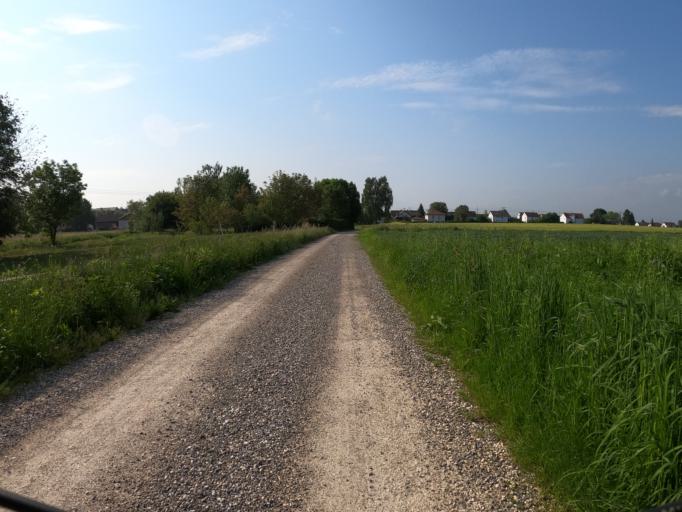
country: DE
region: Bavaria
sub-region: Swabia
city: Pfaffenhofen an der Roth
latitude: 48.3714
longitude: 10.1497
